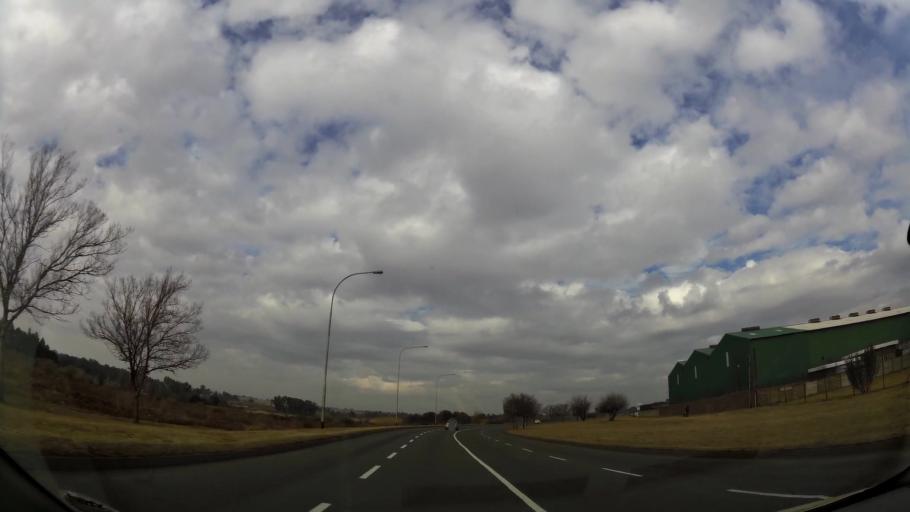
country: ZA
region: Gauteng
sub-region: Sedibeng District Municipality
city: Meyerton
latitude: -26.5753
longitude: 28.0191
